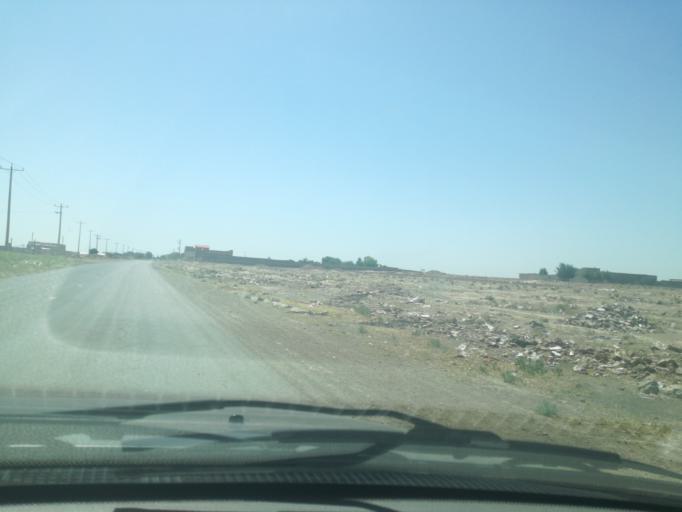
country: IR
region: Razavi Khorasan
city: Sarakhs
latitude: 36.5680
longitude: 61.1394
